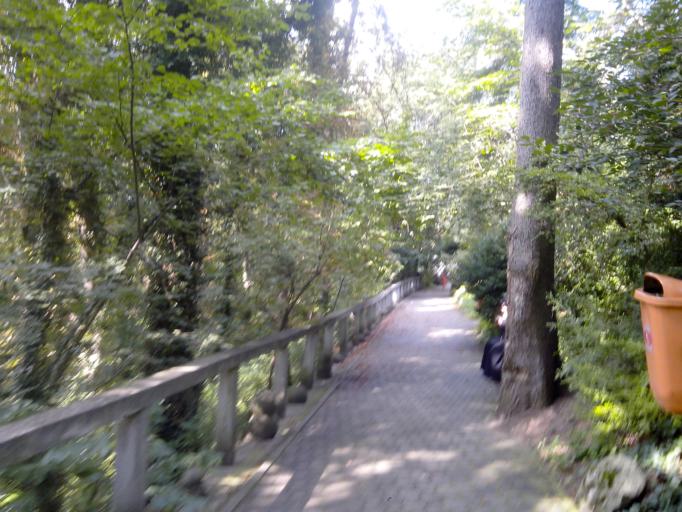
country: RO
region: Cluj
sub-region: Municipiul Cluj-Napoca
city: Cluj-Napoca
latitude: 46.7608
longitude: 23.5868
